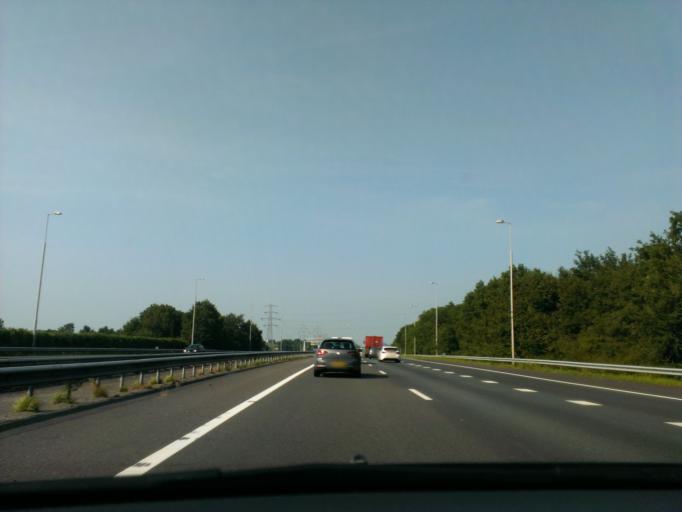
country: NL
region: Gelderland
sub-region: Gemeente Apeldoorn
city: Apeldoorn
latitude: 52.1991
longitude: 6.0191
